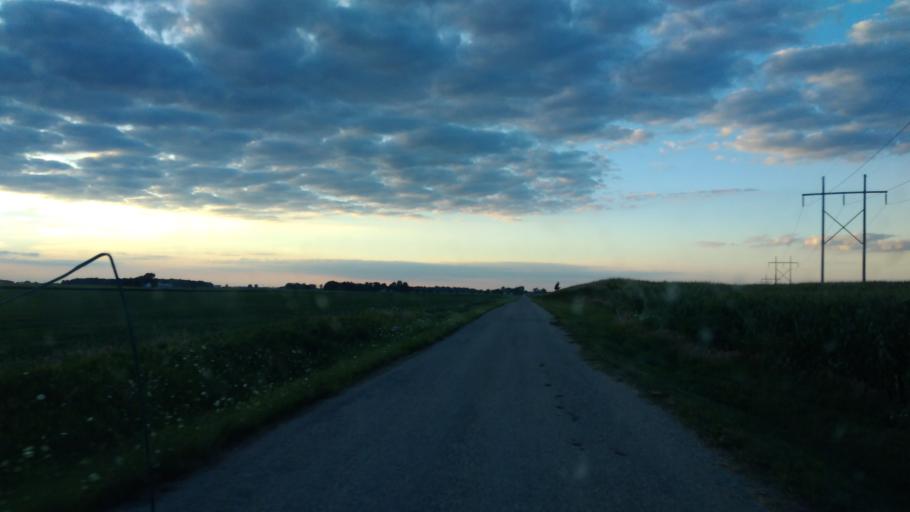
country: US
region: Indiana
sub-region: Adams County
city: Geneva
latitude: 40.6155
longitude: -85.0600
